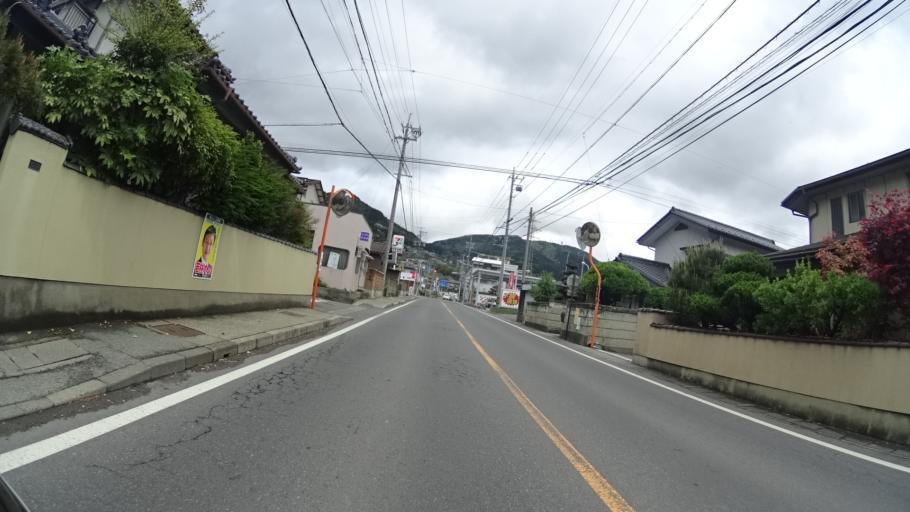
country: JP
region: Nagano
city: Nagano-shi
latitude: 36.6793
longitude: 138.2006
